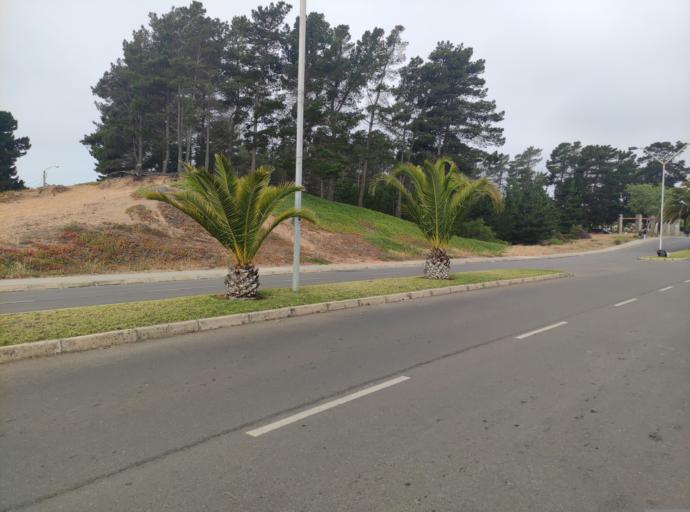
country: CL
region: Valparaiso
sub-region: Provincia de Valparaiso
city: Vina del Mar
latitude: -32.9427
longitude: -71.5414
